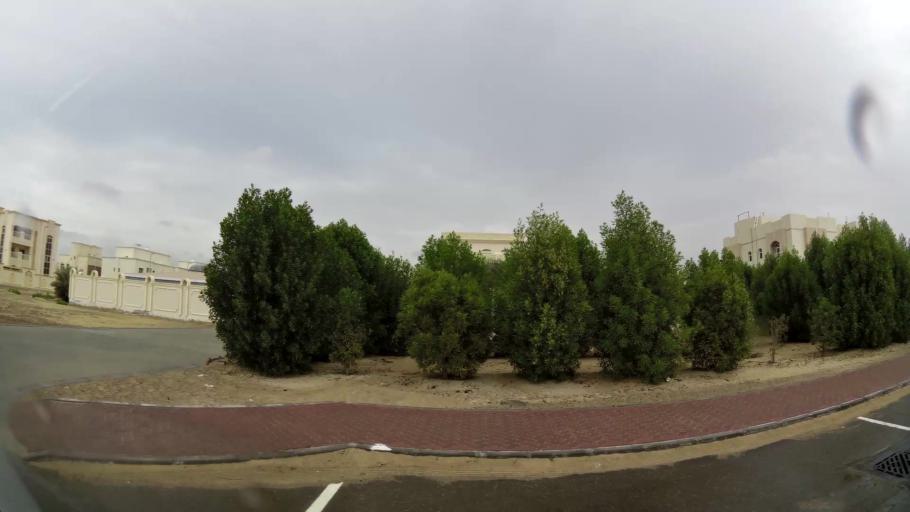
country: AE
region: Abu Dhabi
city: Abu Dhabi
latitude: 24.3572
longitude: 54.6272
